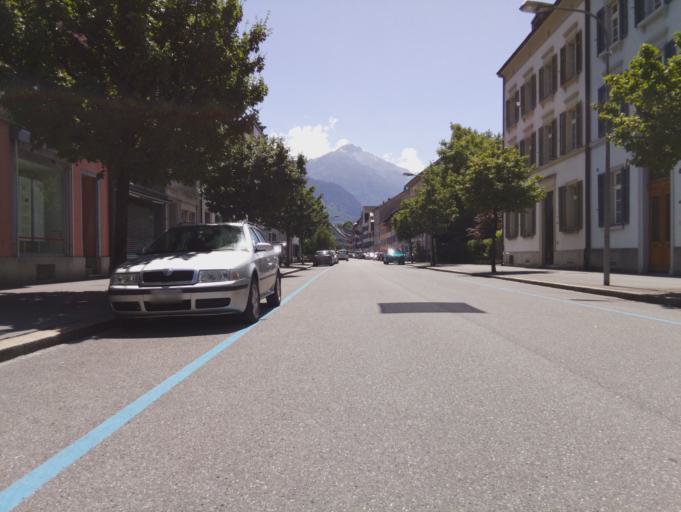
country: CH
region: Glarus
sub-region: Glarus
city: Glarus
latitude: 47.0389
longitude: 9.0687
